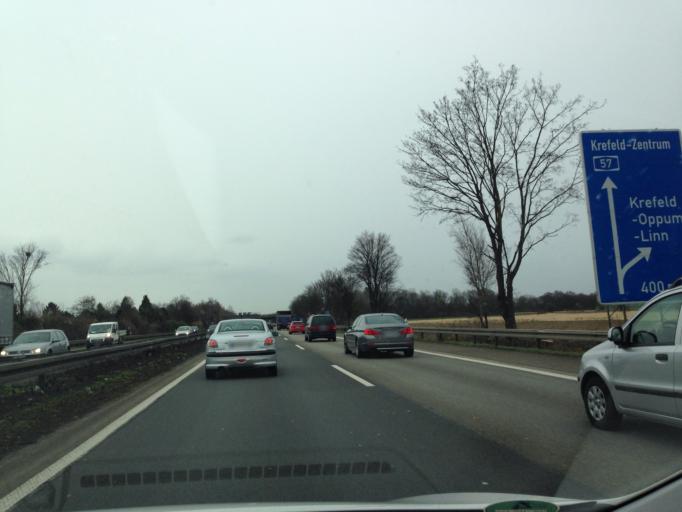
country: DE
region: North Rhine-Westphalia
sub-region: Regierungsbezirk Dusseldorf
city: Krefeld
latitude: 51.3172
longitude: 6.6317
